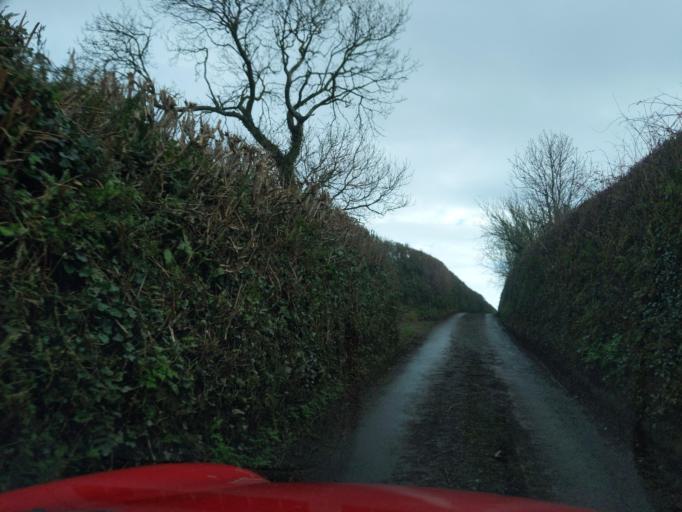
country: GB
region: England
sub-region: Devon
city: Salcombe
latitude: 50.2657
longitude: -3.6913
